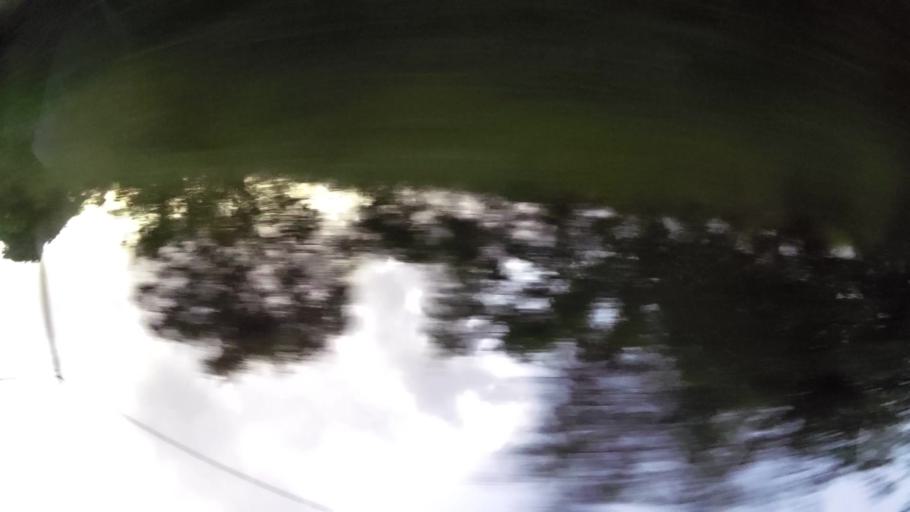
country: BB
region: Saint John
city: Four Cross Roads
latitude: 13.1198
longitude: -59.5167
